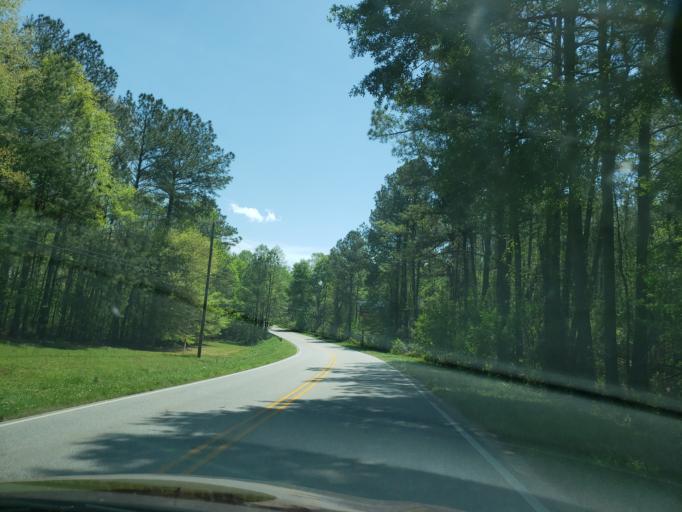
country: US
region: Alabama
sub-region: Lee County
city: Auburn
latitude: 32.6464
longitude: -85.5112
